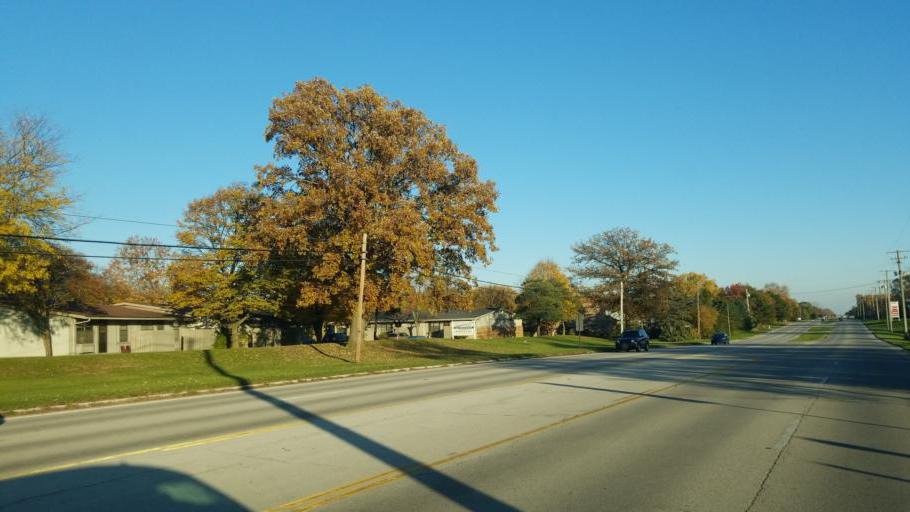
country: US
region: Ohio
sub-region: Sandusky County
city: Fremont
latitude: 41.3385
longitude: -83.0807
